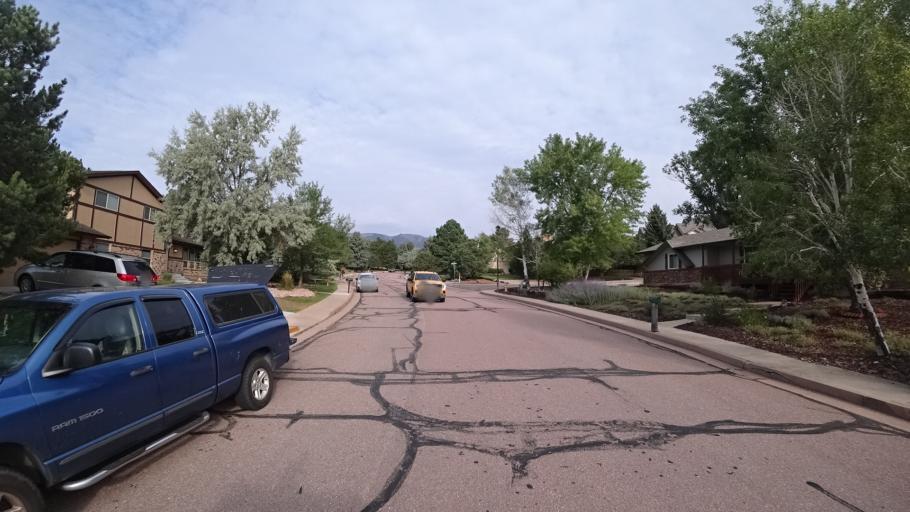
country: US
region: Colorado
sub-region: El Paso County
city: Air Force Academy
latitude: 38.9322
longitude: -104.8463
